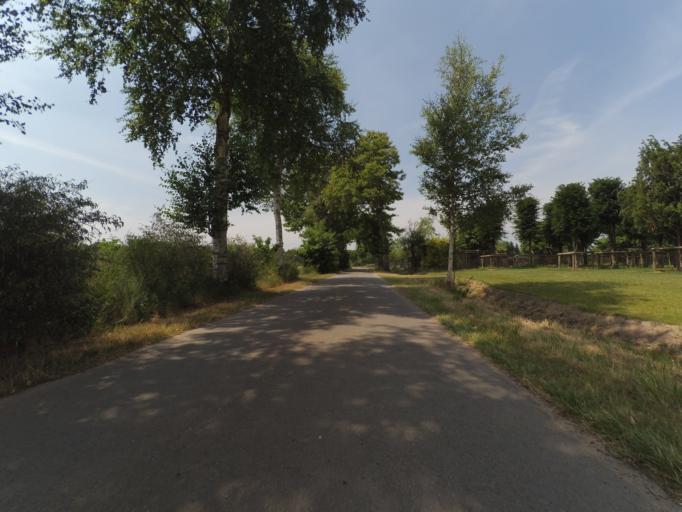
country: BE
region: Flanders
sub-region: Provincie Antwerpen
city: Brecht
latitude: 51.3819
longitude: 4.6358
